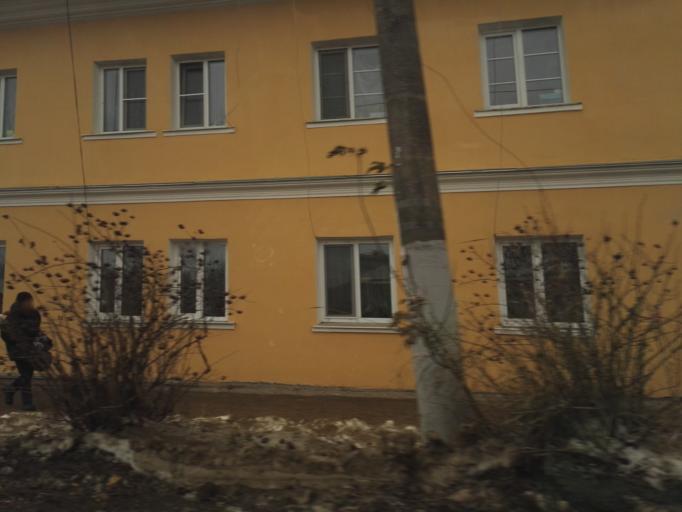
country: RU
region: Tula
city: Tula
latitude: 54.1762
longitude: 37.6258
